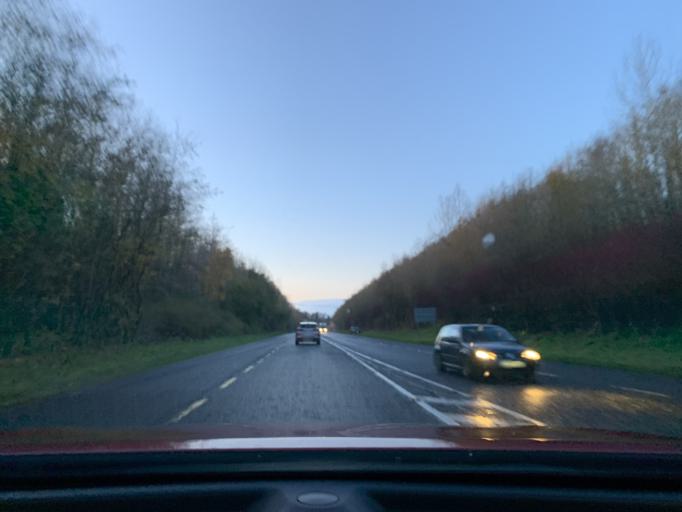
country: IE
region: Connaught
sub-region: County Leitrim
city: Carrick-on-Shannon
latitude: 53.9209
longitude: -7.9890
